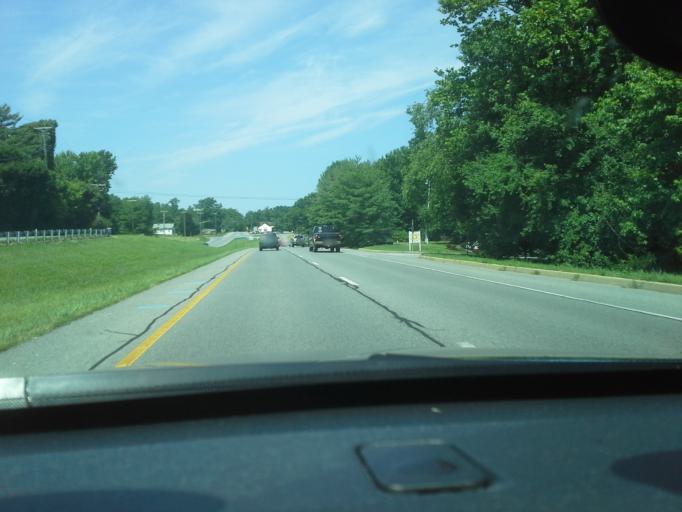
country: US
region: Maryland
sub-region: Calvert County
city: Owings
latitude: 38.7038
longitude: -76.5761
